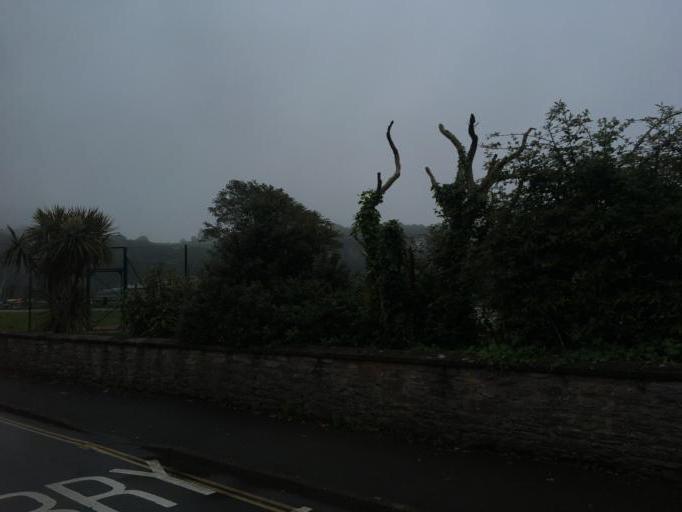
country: GB
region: England
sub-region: Devon
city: Dartmouth
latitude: 50.3552
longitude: -3.5790
